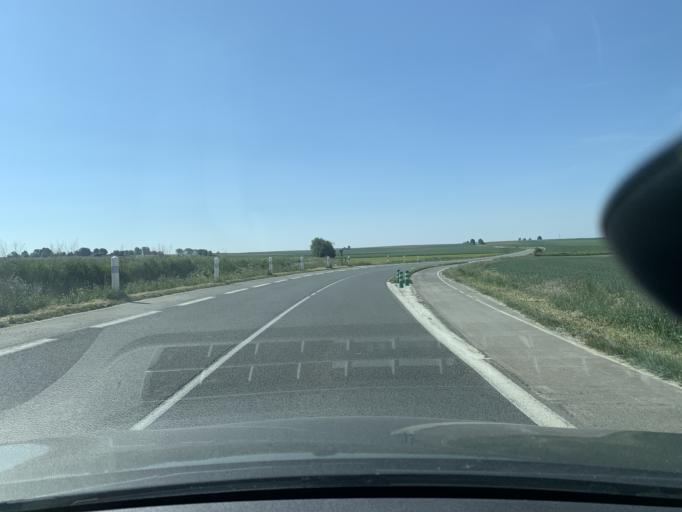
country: FR
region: Nord-Pas-de-Calais
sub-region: Departement du Nord
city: Rumilly-en-Cambresis
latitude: 50.1381
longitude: 3.2467
